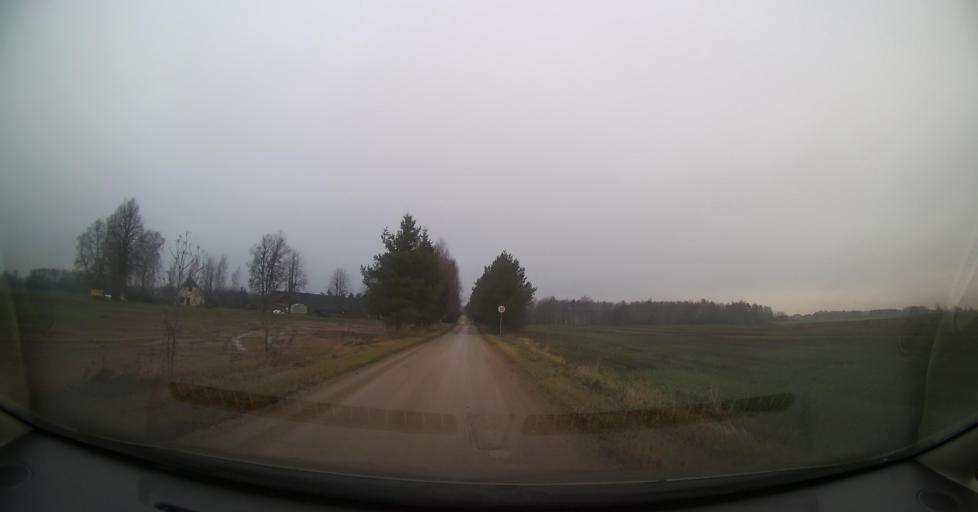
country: EE
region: Tartu
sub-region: Tartu linn
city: Tartu
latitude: 58.3875
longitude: 27.0243
